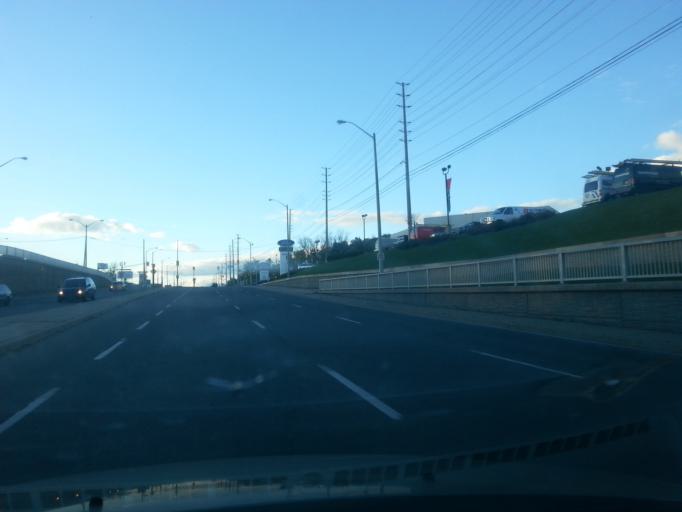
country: CA
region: Ontario
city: Mississauga
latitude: 43.5713
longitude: -79.6409
